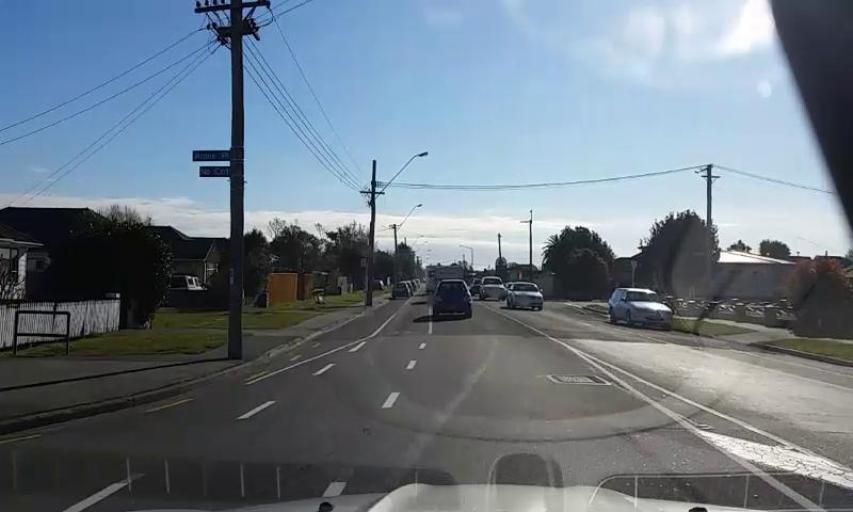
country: NZ
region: Canterbury
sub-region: Christchurch City
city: Christchurch
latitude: -43.5015
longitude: 172.6622
